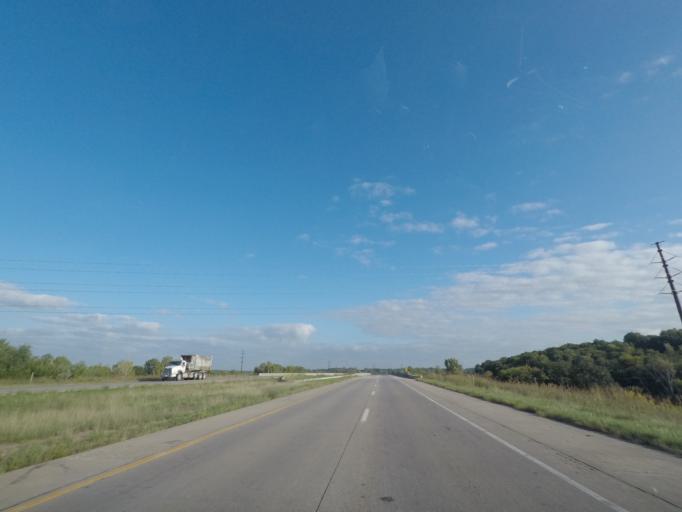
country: US
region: Iowa
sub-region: Polk County
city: Pleasant Hill
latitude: 41.5666
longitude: -93.5119
